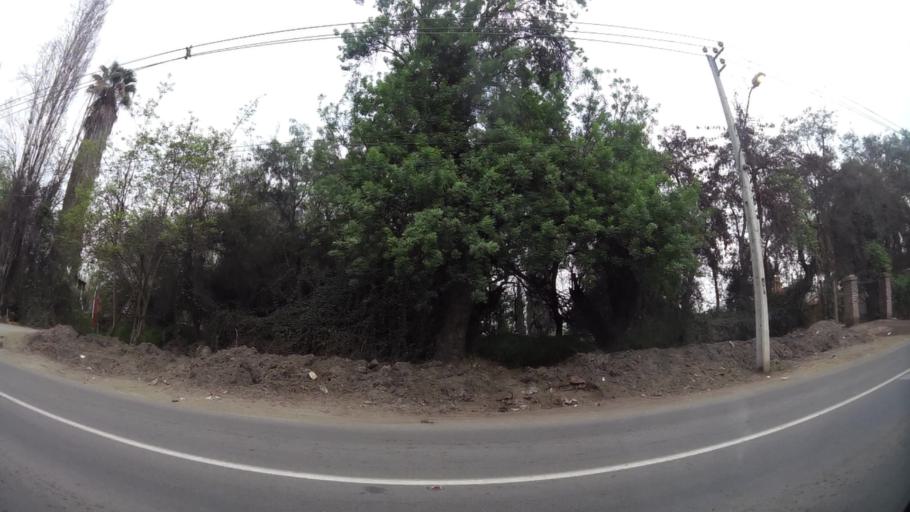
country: CL
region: Santiago Metropolitan
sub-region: Provincia de Chacabuco
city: Chicureo Abajo
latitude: -33.2649
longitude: -70.7543
